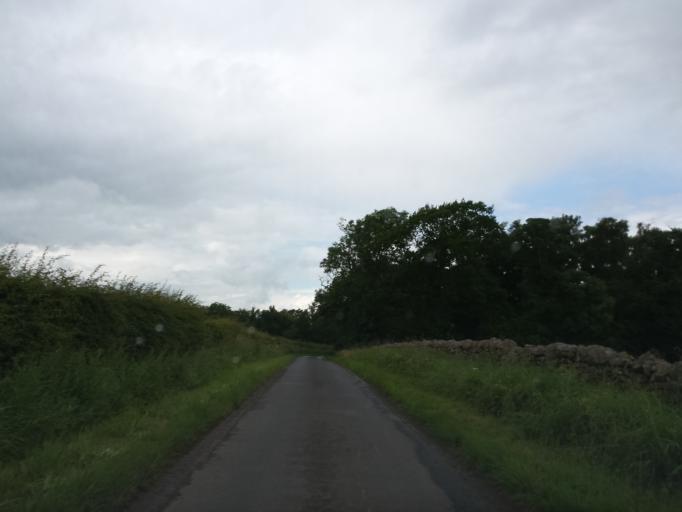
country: GB
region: Scotland
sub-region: The Scottish Borders
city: Saint Boswells
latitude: 55.6081
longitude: -2.5612
